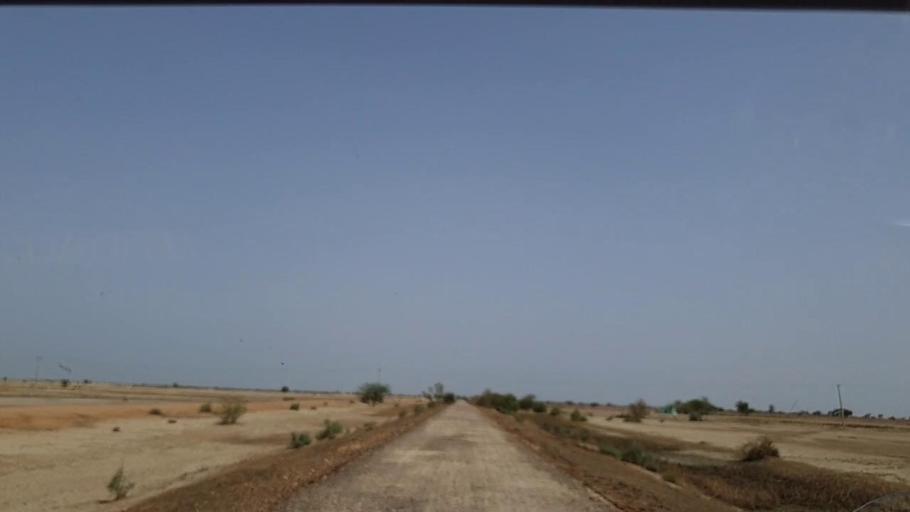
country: PK
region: Sindh
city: Johi
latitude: 26.7726
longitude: 67.6554
